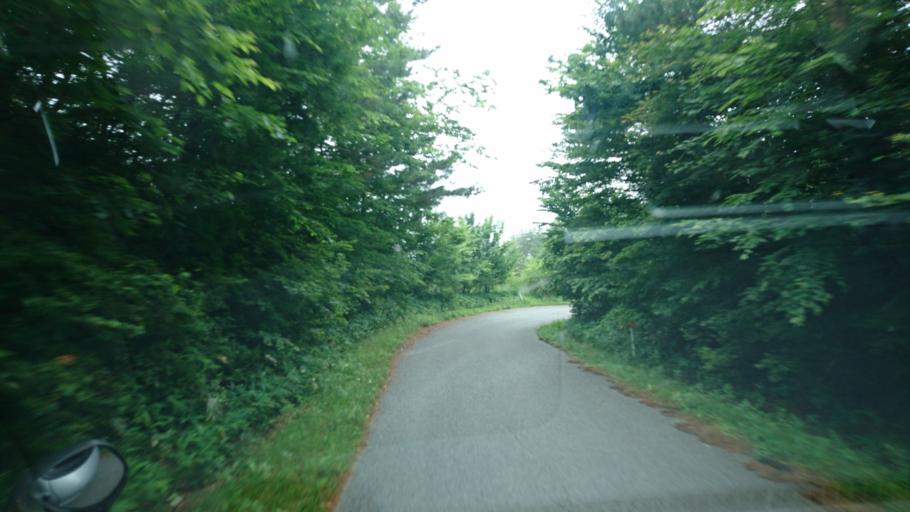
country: JP
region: Iwate
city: Ofunato
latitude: 39.1422
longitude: 141.7539
